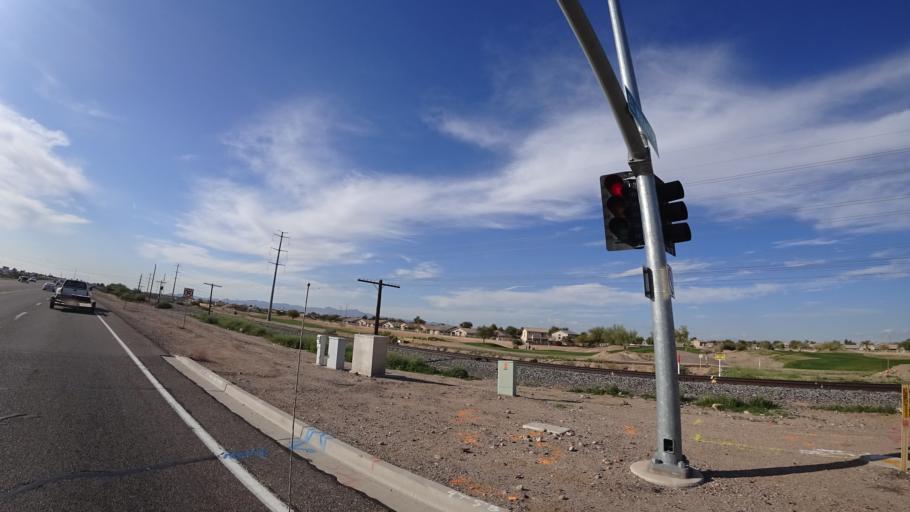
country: US
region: Arizona
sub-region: Maricopa County
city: Avondale
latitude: 33.4354
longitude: -112.3237
